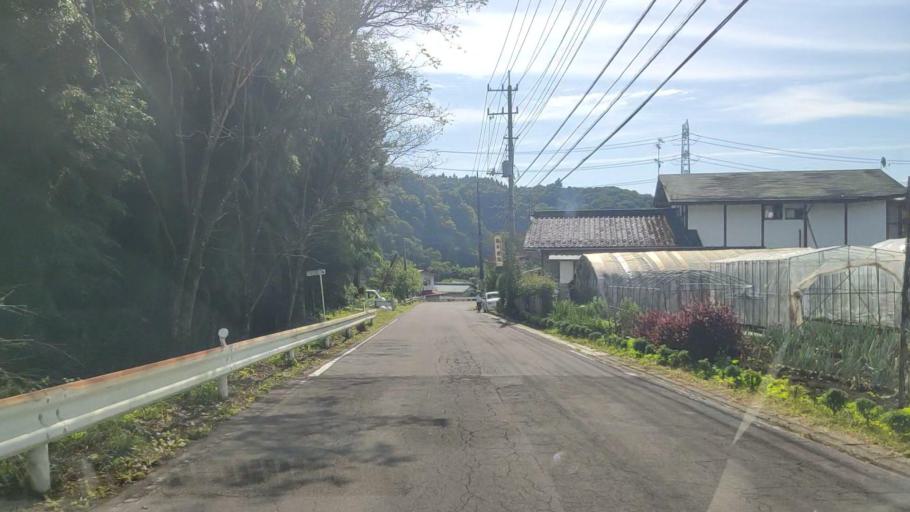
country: JP
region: Gunma
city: Nakanojomachi
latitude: 36.6201
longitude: 138.7783
